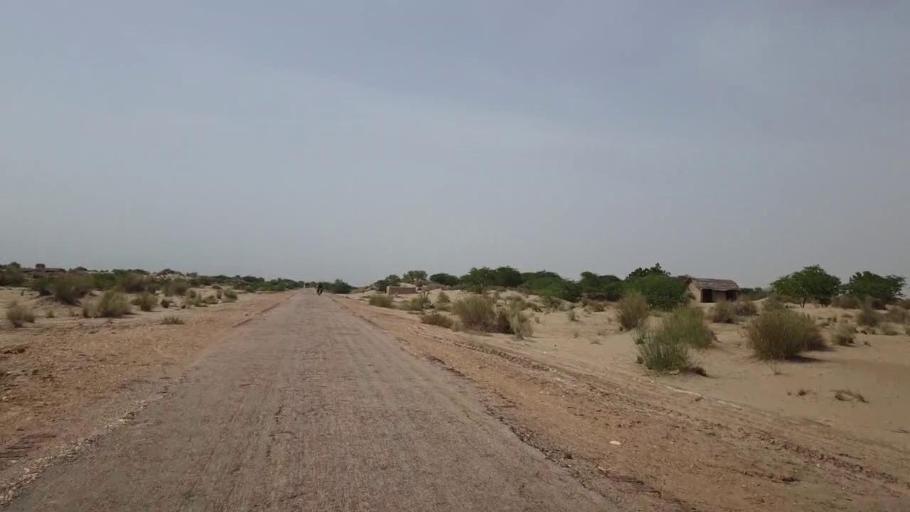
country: PK
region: Sindh
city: Bandhi
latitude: 26.5446
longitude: 68.3855
